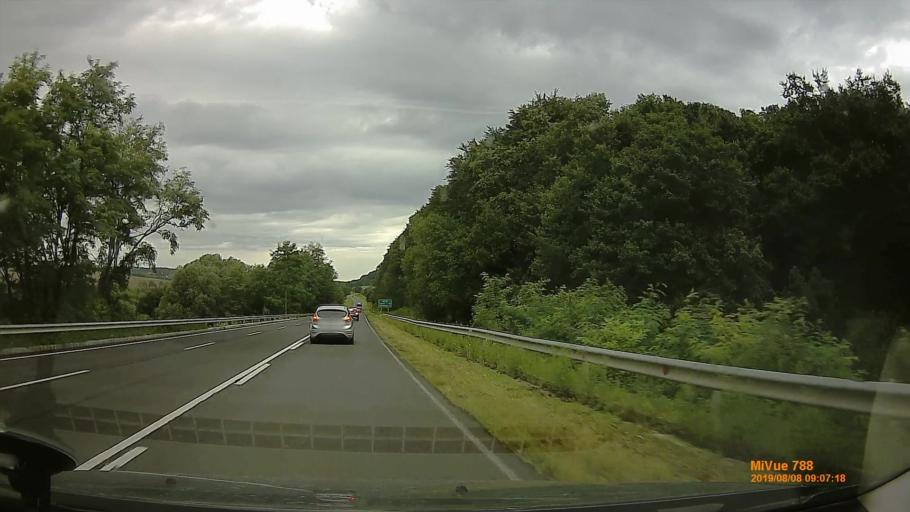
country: HU
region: Zala
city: Zalaegerszeg
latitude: 46.7329
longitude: 16.8561
